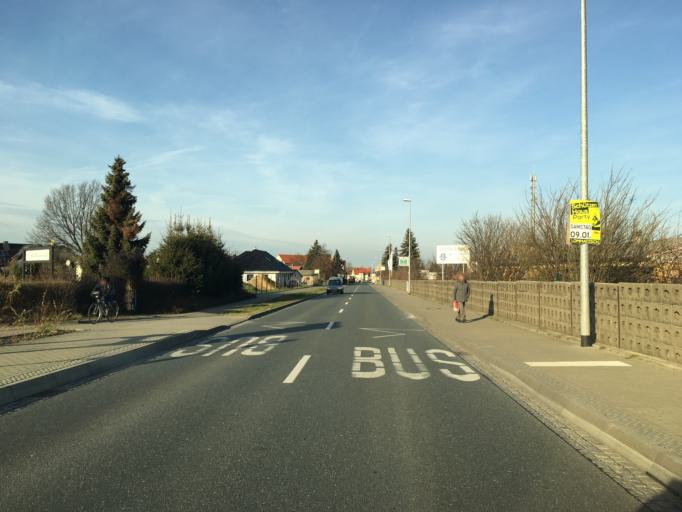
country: DE
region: Saxony
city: Oschatz
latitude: 51.2908
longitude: 13.1226
